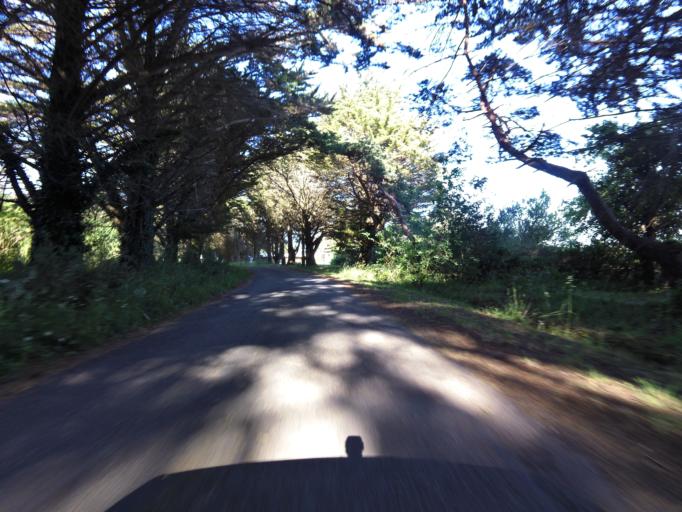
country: FR
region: Brittany
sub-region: Departement du Morbihan
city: Penestin
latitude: 47.4639
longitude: -2.4904
